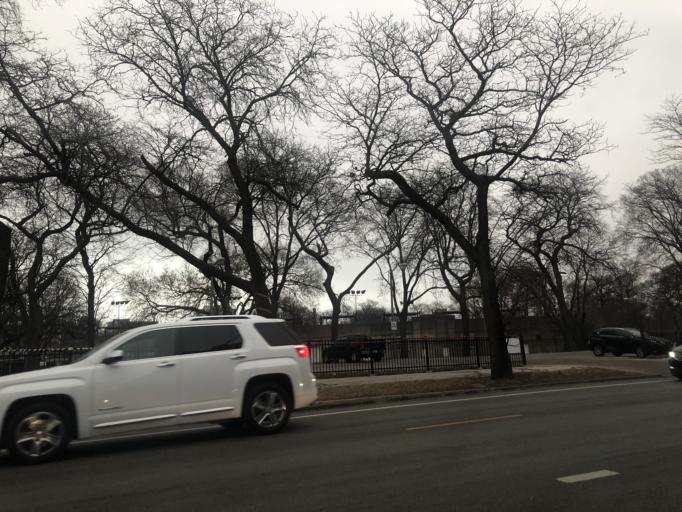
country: US
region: Illinois
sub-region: Cook County
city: Chicago
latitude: 41.7930
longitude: -87.6161
